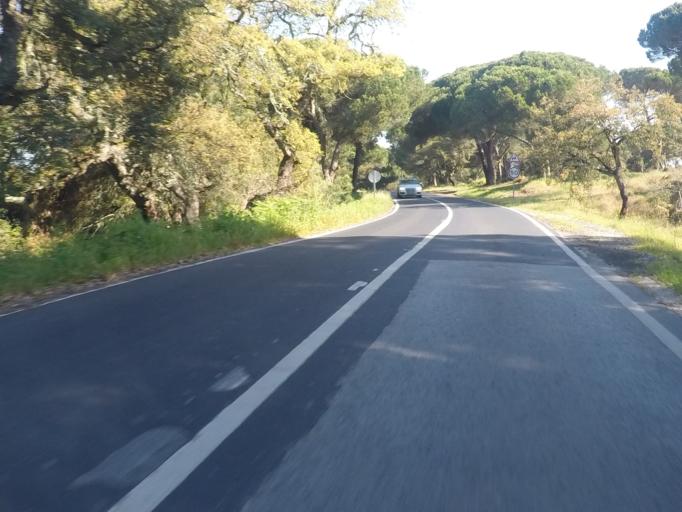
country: PT
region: Setubal
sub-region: Sesimbra
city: Sesimbra
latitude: 38.5073
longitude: -9.1478
